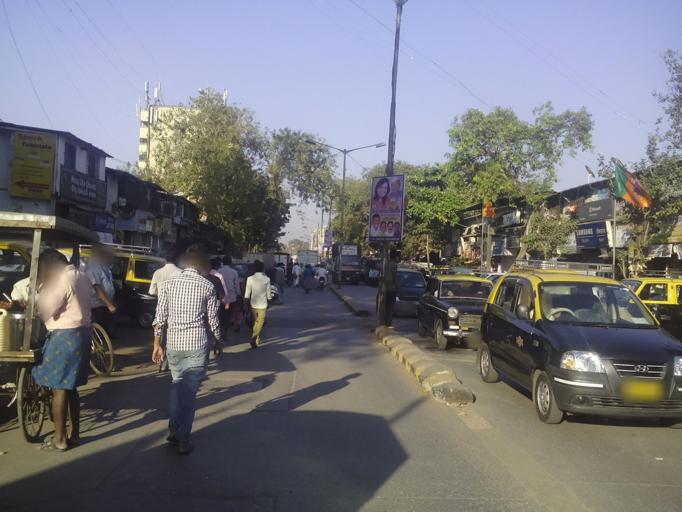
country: IN
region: Maharashtra
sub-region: Mumbai Suburban
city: Mumbai
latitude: 19.0427
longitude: 72.8566
